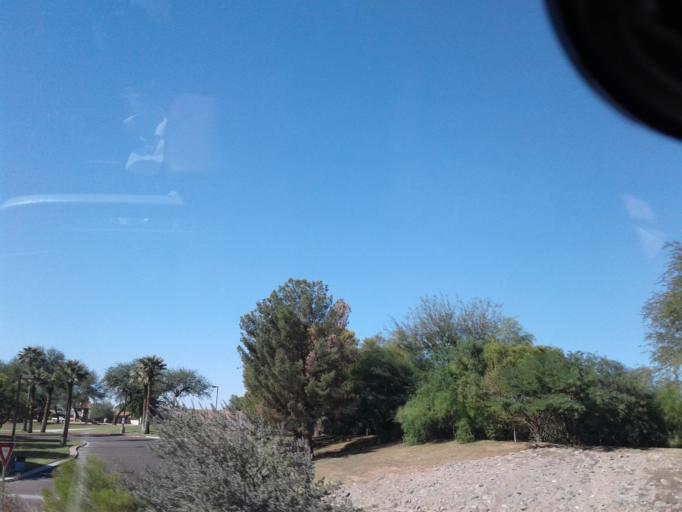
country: US
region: Arizona
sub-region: Maricopa County
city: Scottsdale
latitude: 33.4974
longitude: -111.9097
